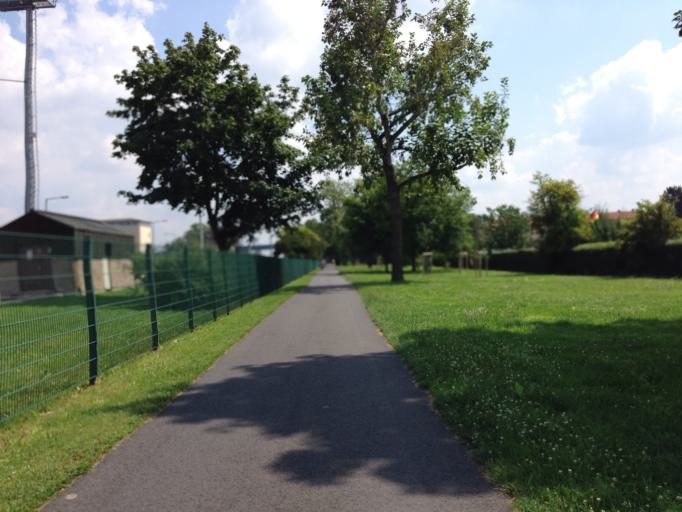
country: DE
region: Hesse
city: Niederrad
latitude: 50.0879
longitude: 8.5960
